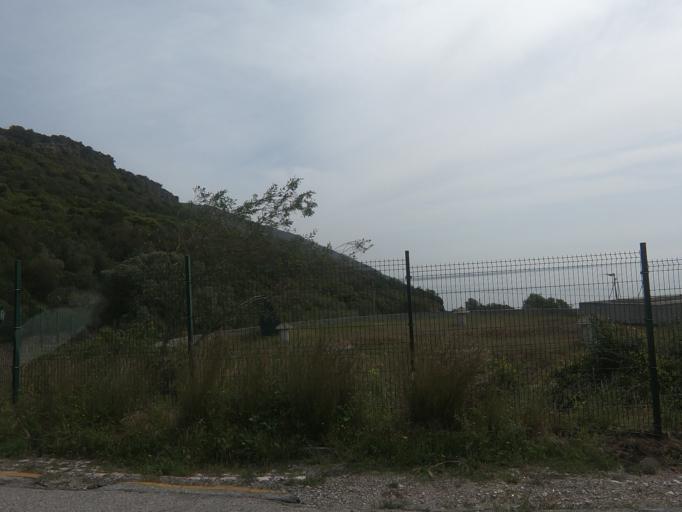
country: PT
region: Setubal
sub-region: Palmela
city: Quinta do Anjo
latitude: 38.4847
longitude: -8.9731
